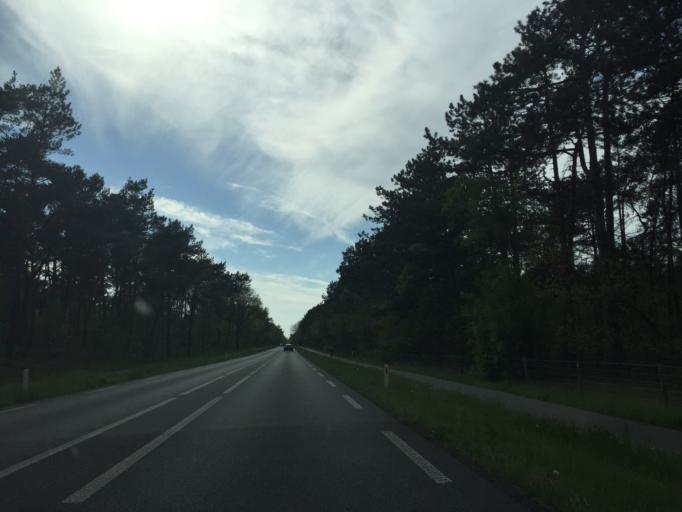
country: NL
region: Gelderland
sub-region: Gemeente Apeldoorn
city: Uddel
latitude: 52.2216
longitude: 5.7928
